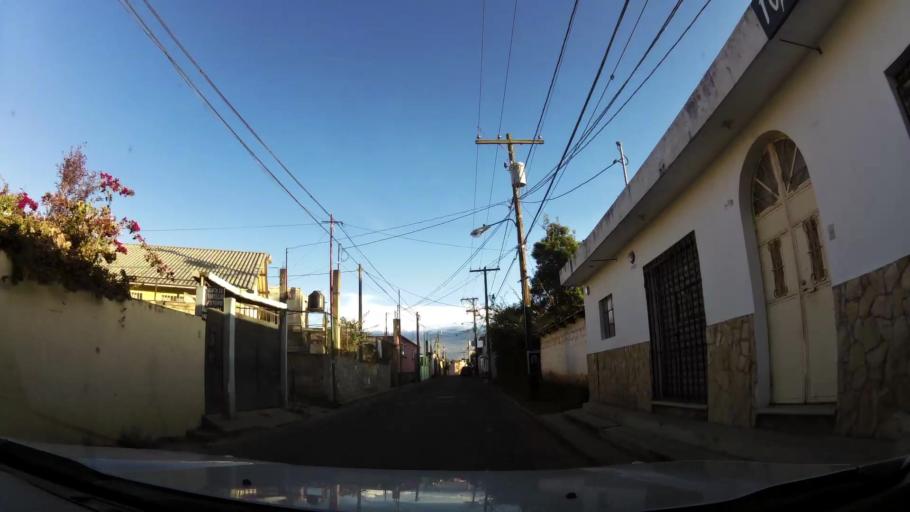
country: GT
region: Sacatepequez
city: San Lucas Sacatepequez
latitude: 14.6143
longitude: -90.6571
